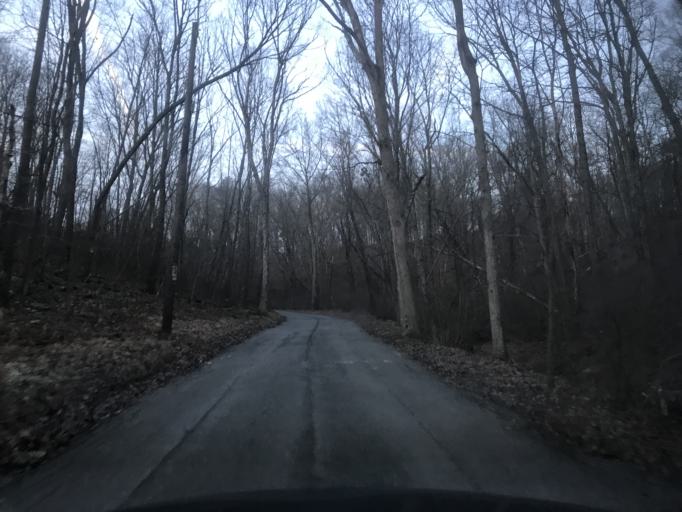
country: US
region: Pennsylvania
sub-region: York County
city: New Freedom
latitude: 39.6803
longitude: -76.7049
